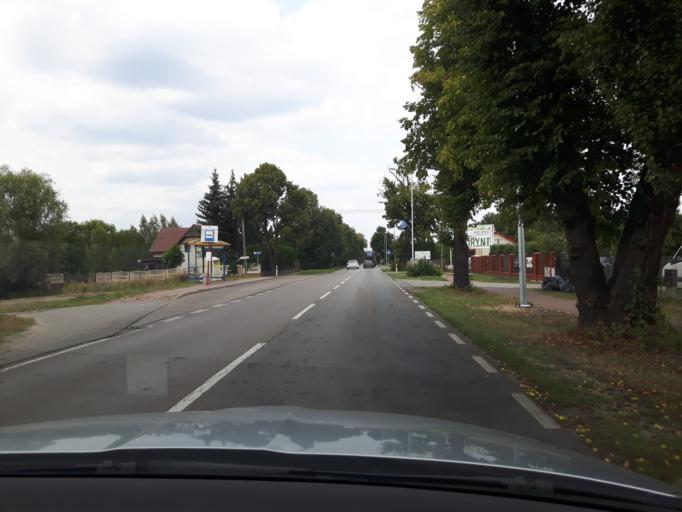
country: PL
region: Masovian Voivodeship
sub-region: Powiat legionowski
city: Nieporet
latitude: 52.4069
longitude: 21.0385
